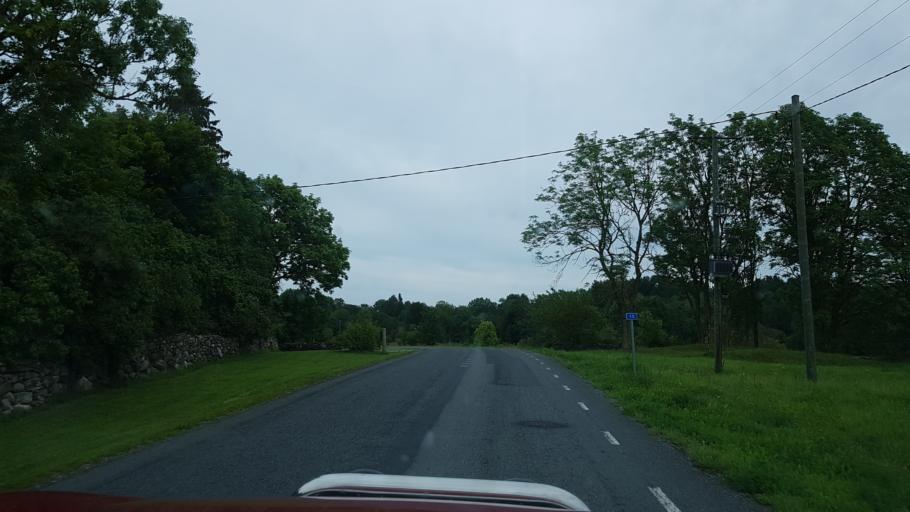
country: EE
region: Laeaene
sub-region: Lihula vald
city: Lihula
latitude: 58.8755
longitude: 23.8696
